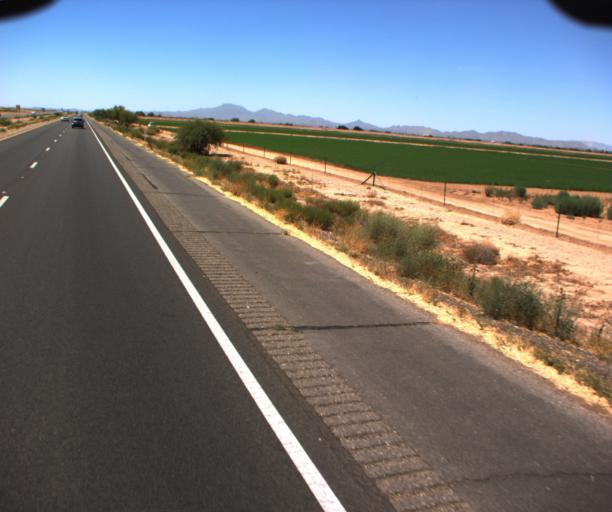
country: US
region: Arizona
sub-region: Pinal County
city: Maricopa
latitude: 33.0215
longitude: -112.0480
